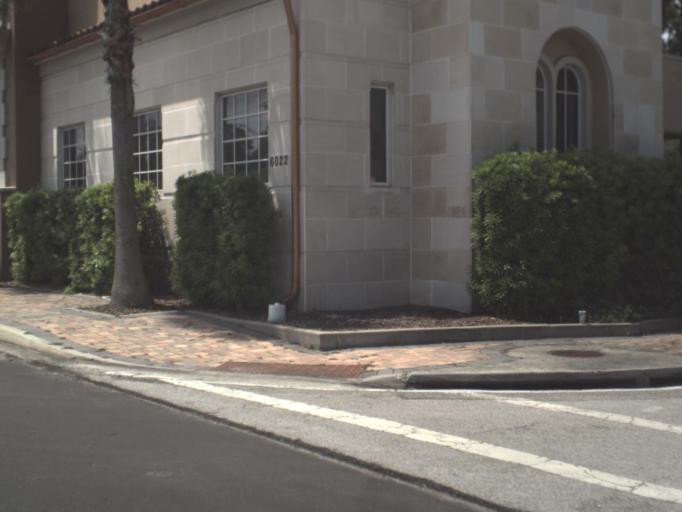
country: US
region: Florida
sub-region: Duval County
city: Jacksonville
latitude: 30.2603
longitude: -81.6451
